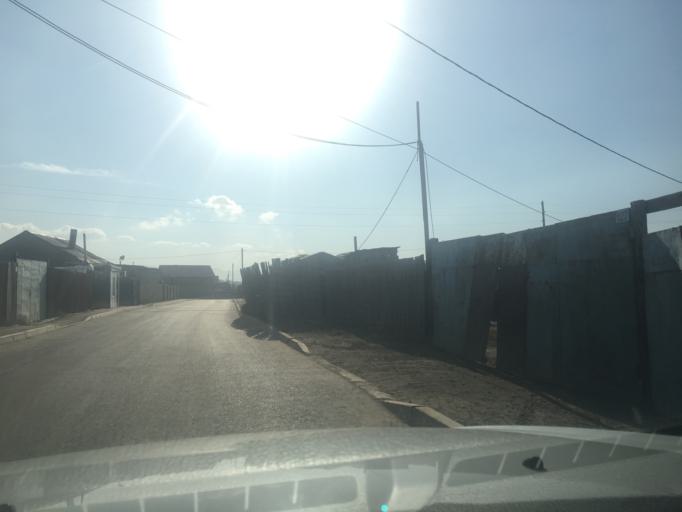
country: MN
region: Ulaanbaatar
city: Ulaanbaatar
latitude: 47.9663
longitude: 106.8270
